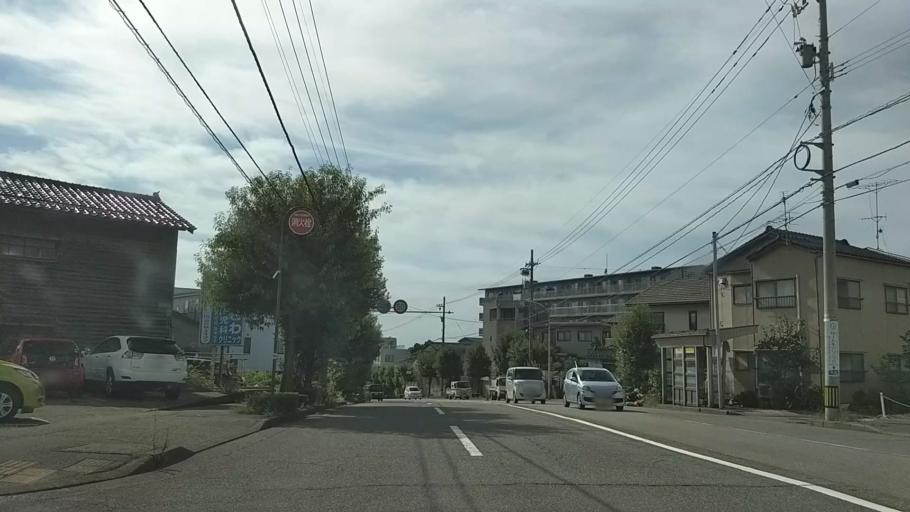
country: JP
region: Ishikawa
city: Nonoichi
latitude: 36.5529
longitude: 136.6687
